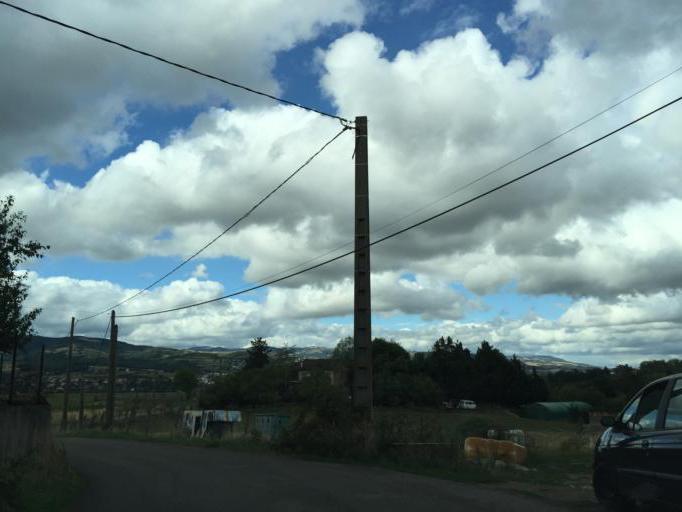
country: FR
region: Rhone-Alpes
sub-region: Departement de la Loire
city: Saint-Paul-en-Jarez
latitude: 45.4761
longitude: 4.5510
